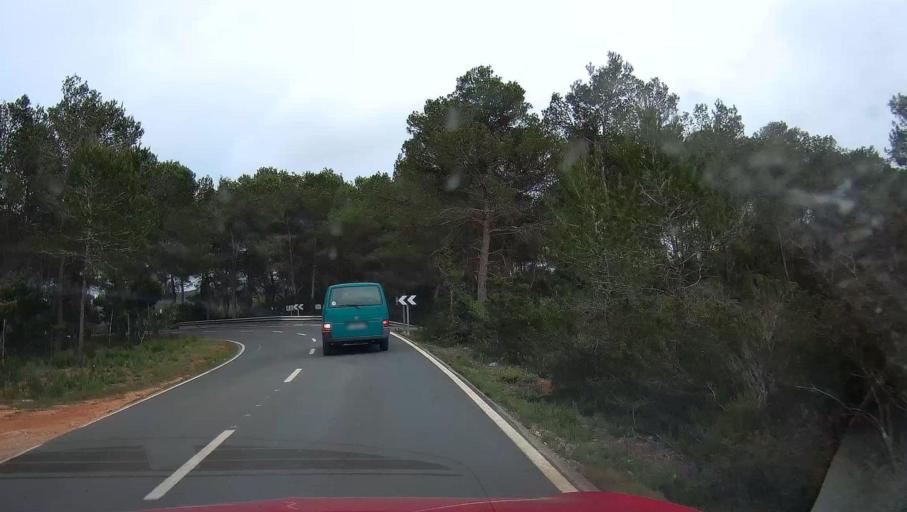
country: ES
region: Balearic Islands
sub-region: Illes Balears
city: Sant Joan de Labritja
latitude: 39.0468
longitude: 1.4097
